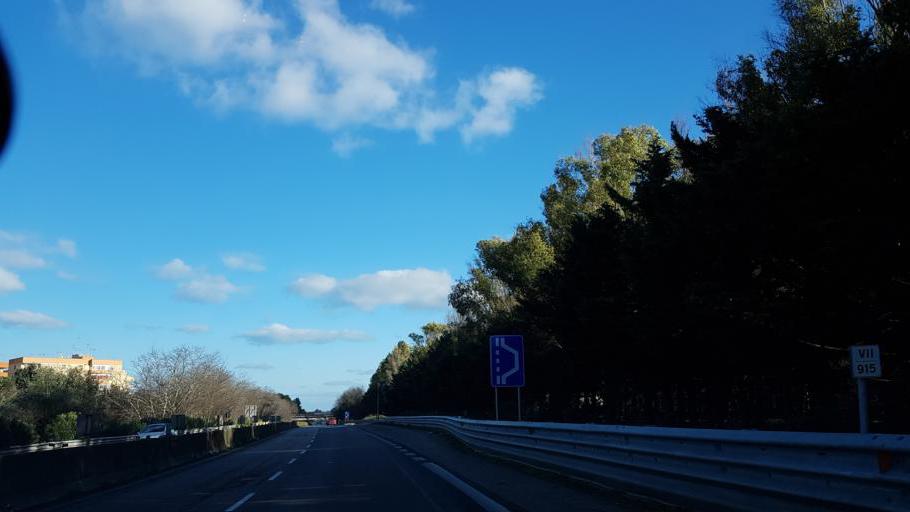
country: IT
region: Apulia
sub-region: Provincia di Brindisi
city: Brindisi
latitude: 40.6208
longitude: 17.9284
